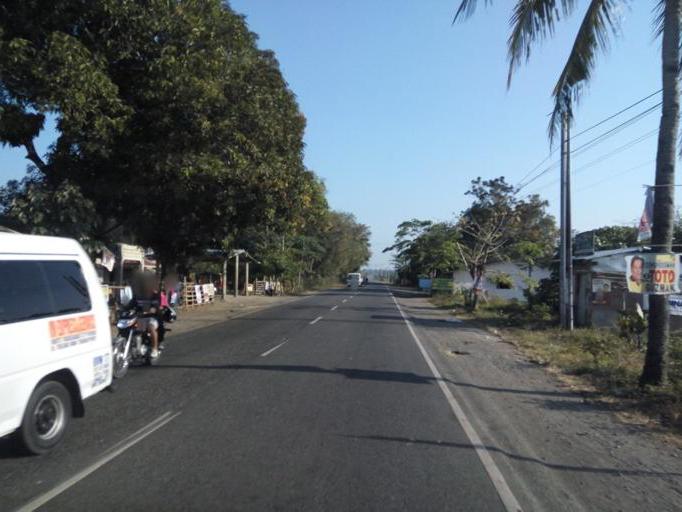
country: PH
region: Cagayan Valley
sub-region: Province of Cagayan
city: Iguig
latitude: 17.7338
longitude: 121.7385
